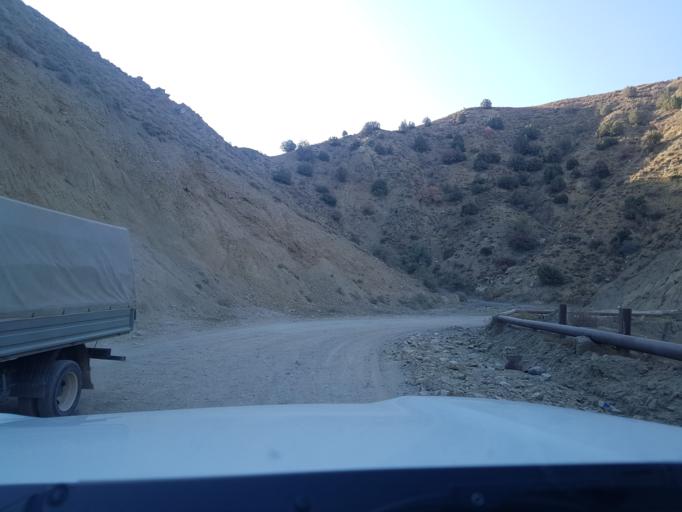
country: TM
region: Ahal
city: Baharly
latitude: 38.4420
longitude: 57.0481
